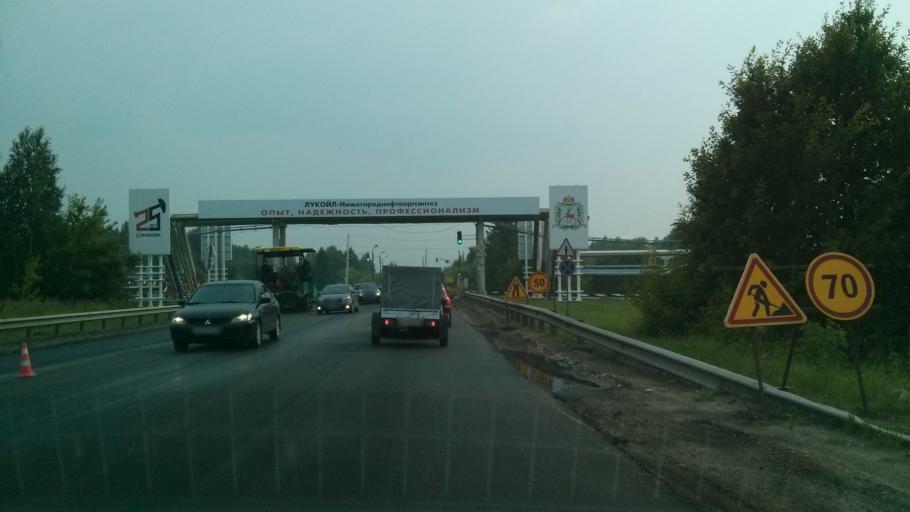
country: RU
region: Nizjnij Novgorod
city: Kstovo
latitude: 56.1152
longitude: 44.1508
